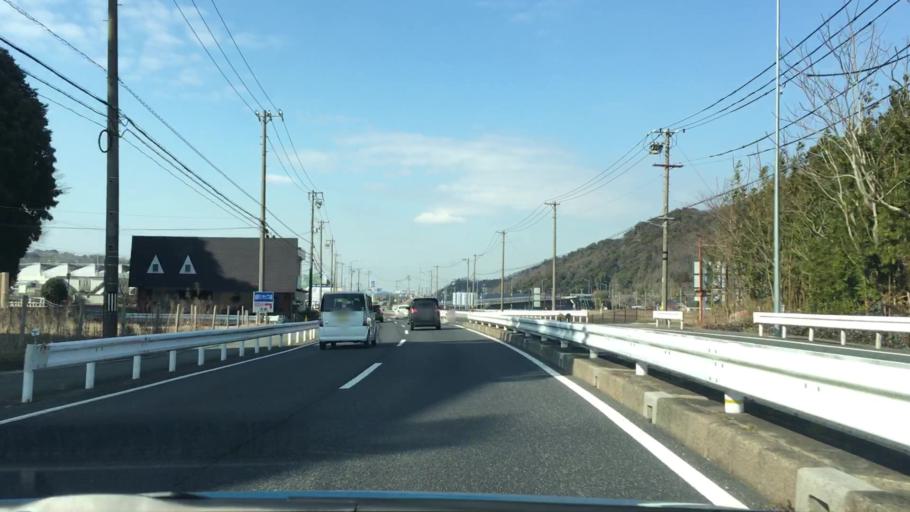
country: JP
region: Aichi
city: Gamagori
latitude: 34.9058
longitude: 137.2333
